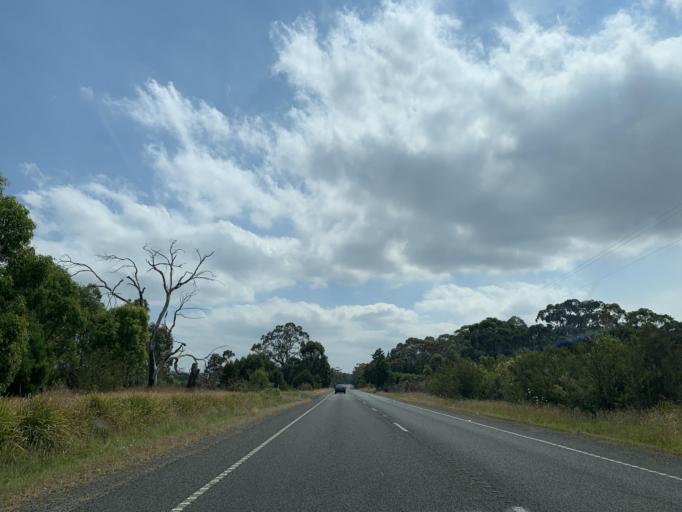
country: AU
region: Victoria
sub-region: Latrobe
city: Morwell
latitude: -38.2031
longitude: 146.4649
